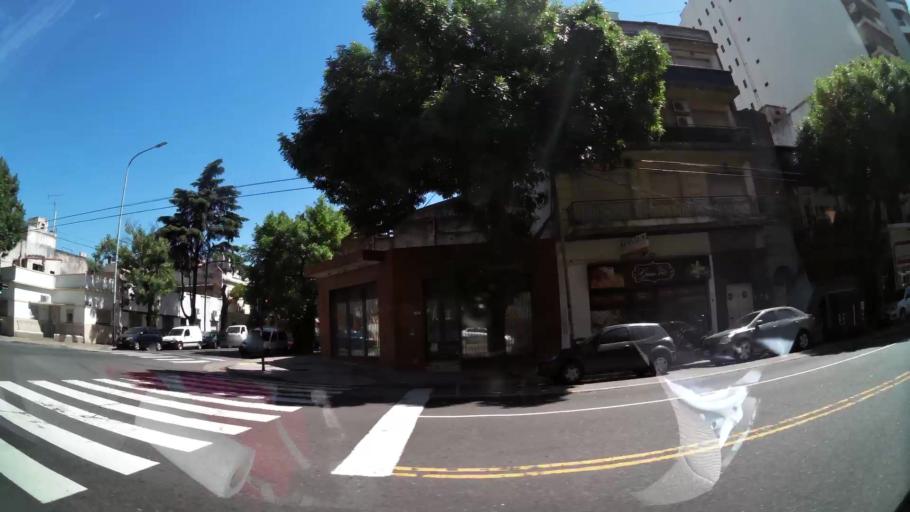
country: AR
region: Buenos Aires F.D.
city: Buenos Aires
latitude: -34.6304
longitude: -58.4175
